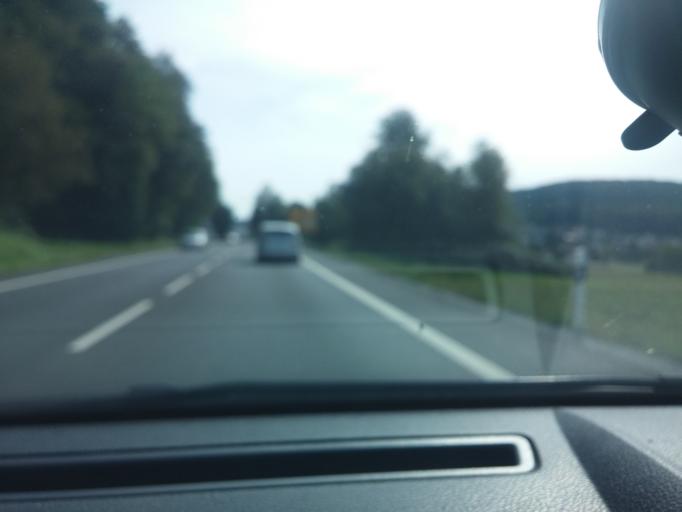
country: DE
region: Hesse
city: Hochst im Odenwald
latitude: 49.7745
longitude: 8.9922
